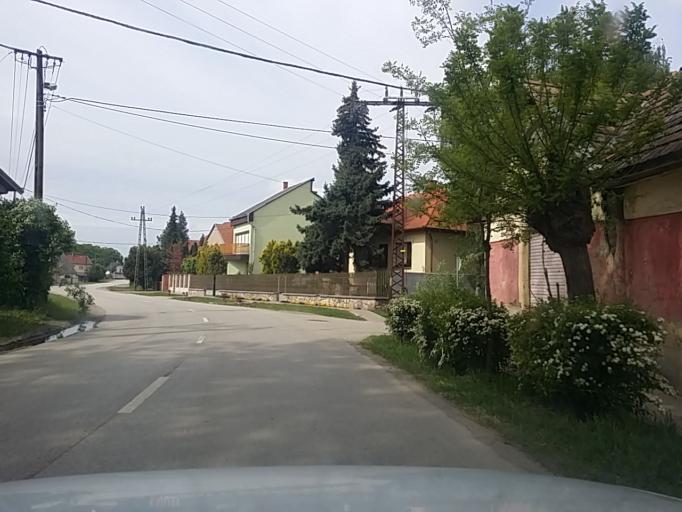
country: HU
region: Pest
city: Szentlorinckata
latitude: 47.5089
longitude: 19.7798
